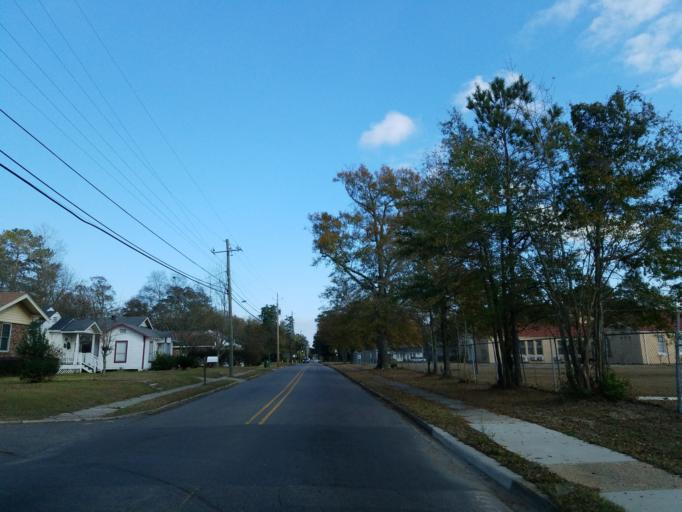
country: US
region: Mississippi
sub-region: Forrest County
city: Hattiesburg
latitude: 31.3357
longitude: -89.3043
